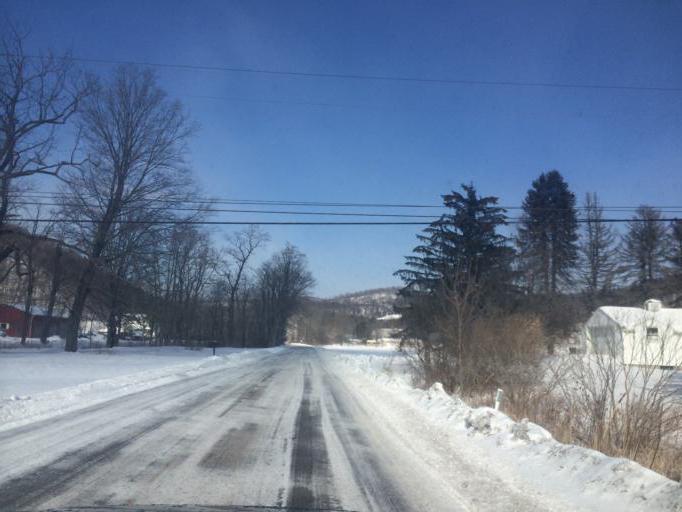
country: US
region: Pennsylvania
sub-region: Centre County
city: Stormstown
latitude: 40.8394
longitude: -77.9959
